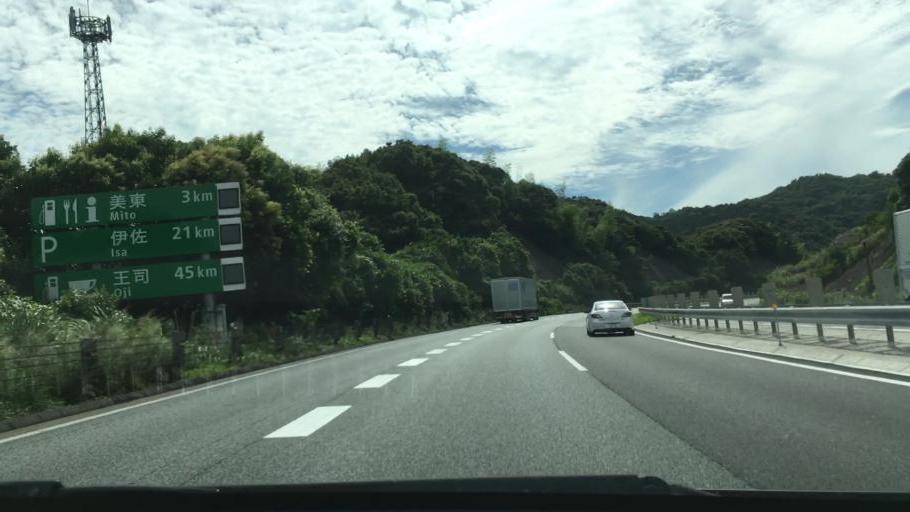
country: JP
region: Yamaguchi
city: Ogori-shimogo
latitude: 34.1358
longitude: 131.3679
